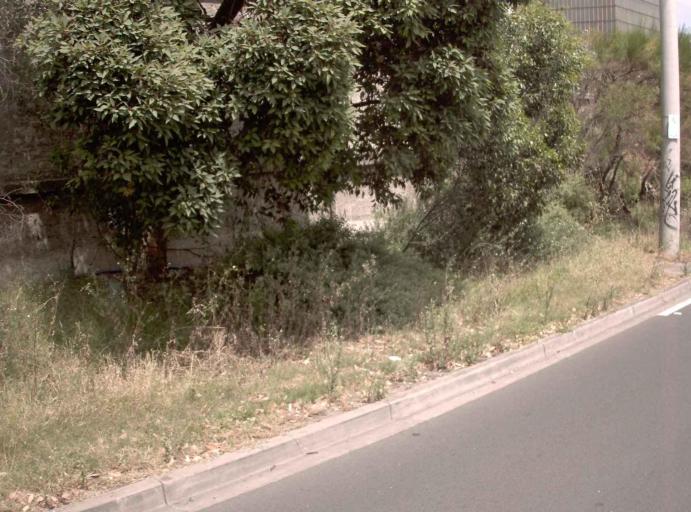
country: AU
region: Victoria
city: Alphington
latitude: -37.7844
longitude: 145.0253
